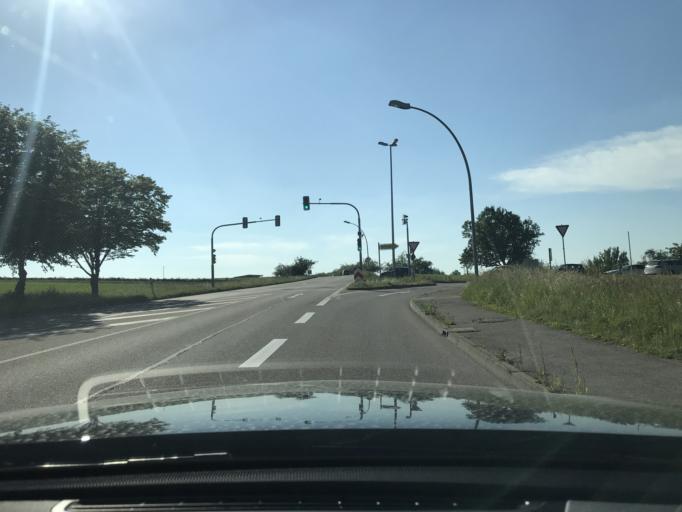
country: DE
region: Baden-Wuerttemberg
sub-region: Regierungsbezirk Stuttgart
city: Weinstadt-Endersbach
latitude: 48.8156
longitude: 9.3485
